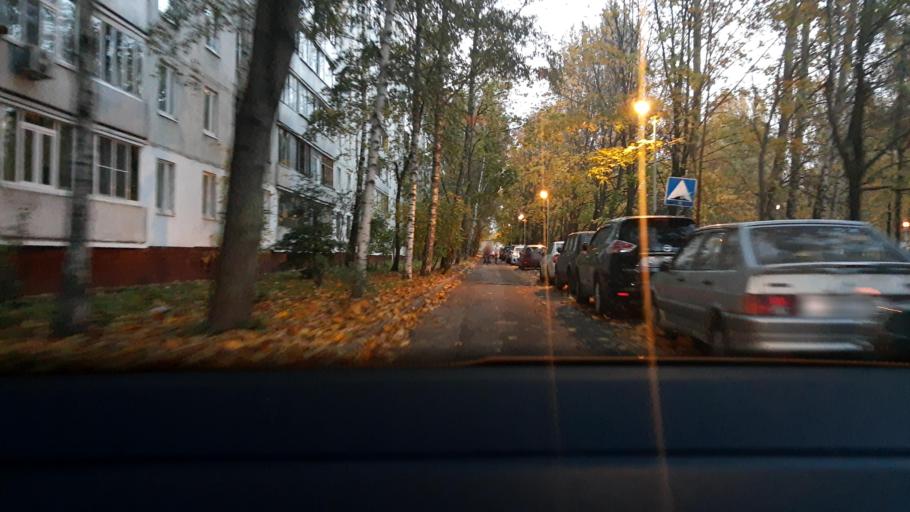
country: RU
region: Moscow
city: Kozeyevo
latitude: 55.8722
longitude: 37.6111
